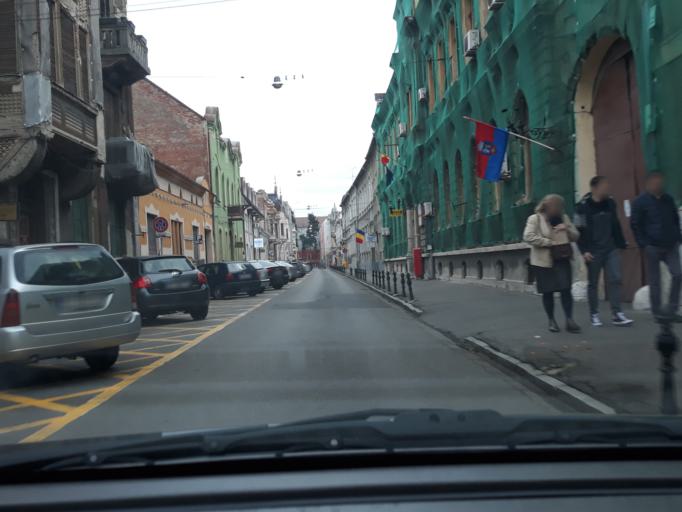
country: RO
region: Bihor
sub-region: Comuna Biharea
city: Oradea
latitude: 47.0599
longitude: 21.9319
